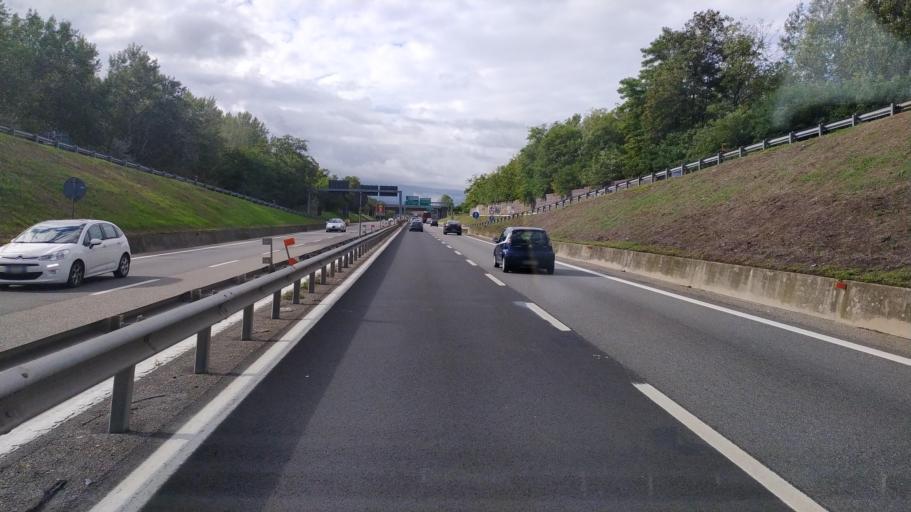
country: IT
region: Lombardy
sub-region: Provincia di Pavia
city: Pavia
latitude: 45.1987
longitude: 9.1381
